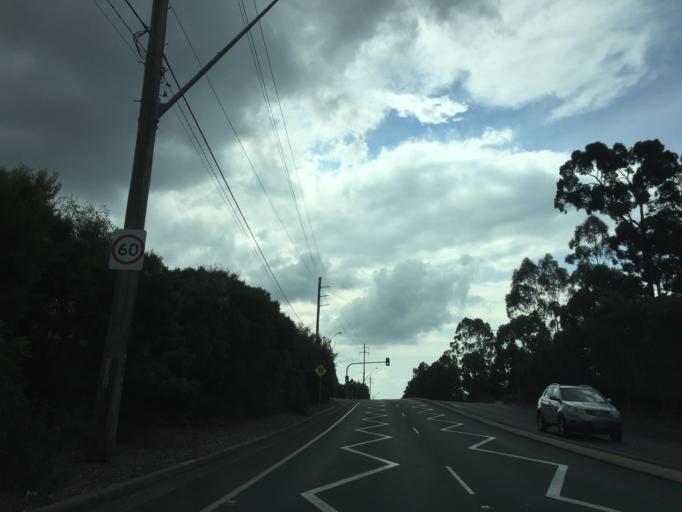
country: AU
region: New South Wales
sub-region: The Hills Shire
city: Glenhaven
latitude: -33.7072
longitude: 150.9731
